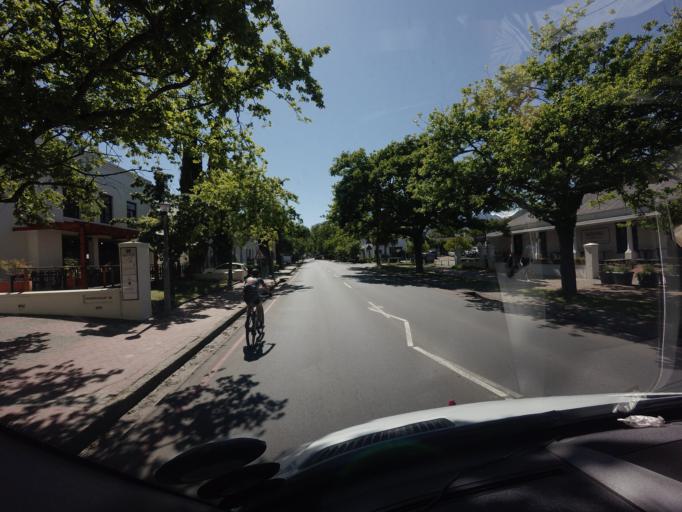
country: ZA
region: Western Cape
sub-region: Cape Winelands District Municipality
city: Stellenbosch
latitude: -33.9396
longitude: 18.8562
